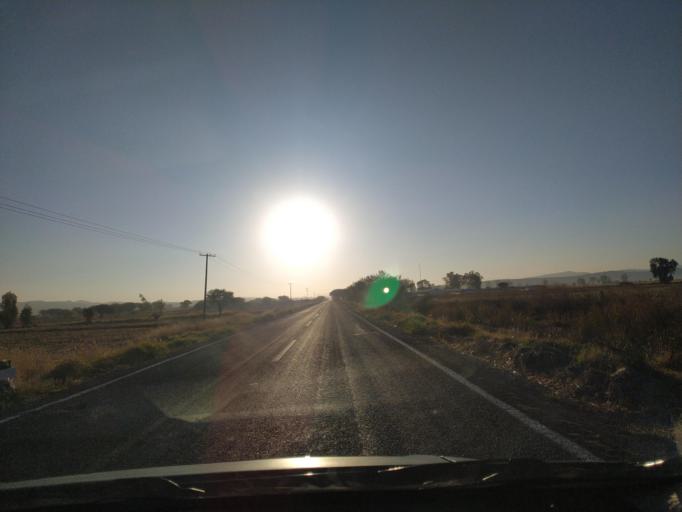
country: MX
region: Guanajuato
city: Ciudad Manuel Doblado
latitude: 20.7387
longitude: -101.8736
